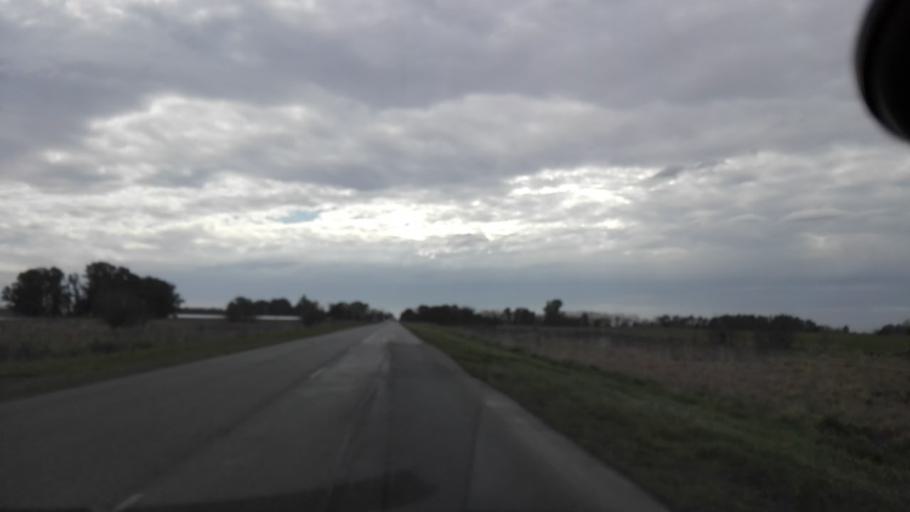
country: AR
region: Buenos Aires
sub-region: Partido de Las Flores
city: Las Flores
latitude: -36.2291
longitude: -59.0446
